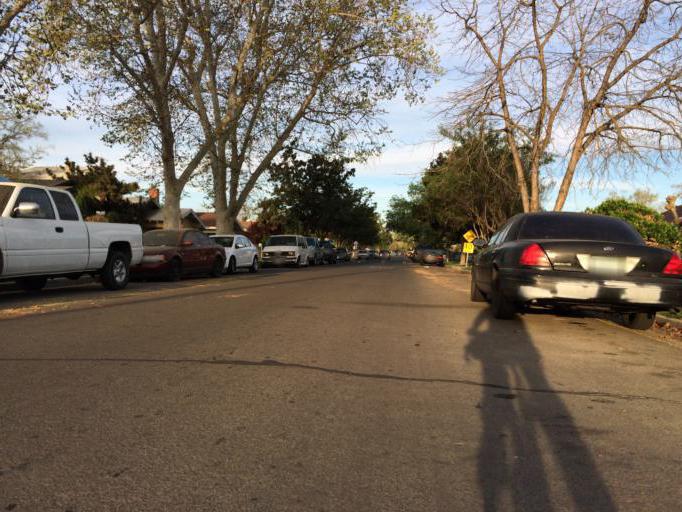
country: US
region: California
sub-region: Fresno County
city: Fresno
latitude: 36.7450
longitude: -119.7609
